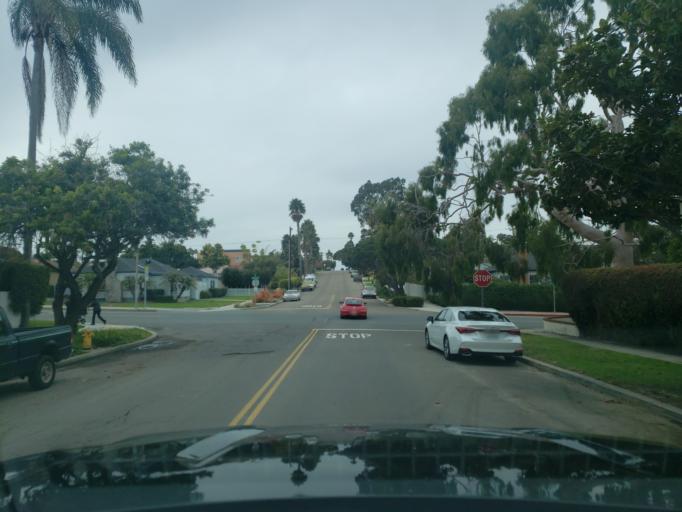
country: US
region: California
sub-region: San Diego County
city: Coronado
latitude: 32.7331
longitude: -117.2414
